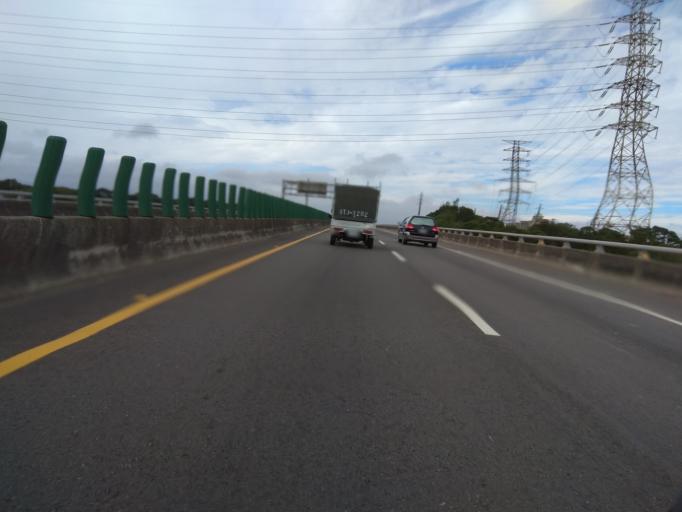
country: TW
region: Taiwan
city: Daxi
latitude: 24.8988
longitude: 121.2536
